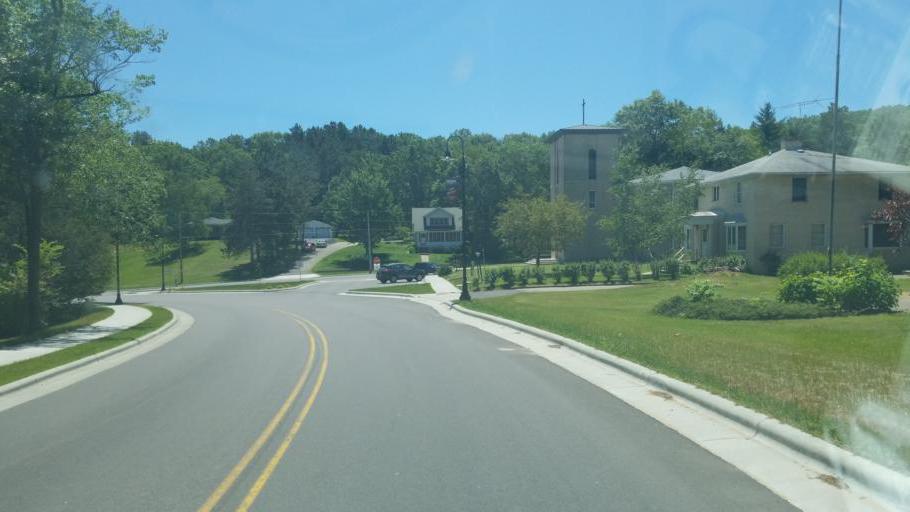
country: US
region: Wisconsin
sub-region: Juneau County
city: New Lisbon
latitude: 43.9213
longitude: -90.2719
